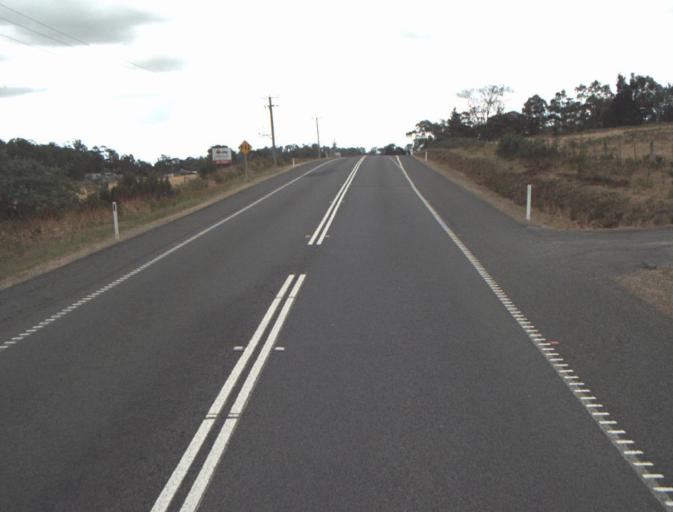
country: AU
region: Tasmania
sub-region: Launceston
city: Mayfield
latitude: -41.2520
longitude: 147.0225
